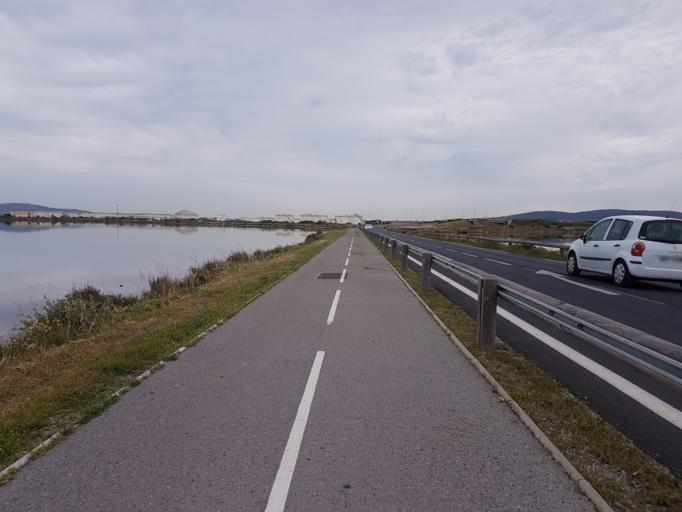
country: FR
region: Languedoc-Roussillon
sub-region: Departement de l'Herault
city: Frontignan
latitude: 43.4357
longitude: 3.7682
